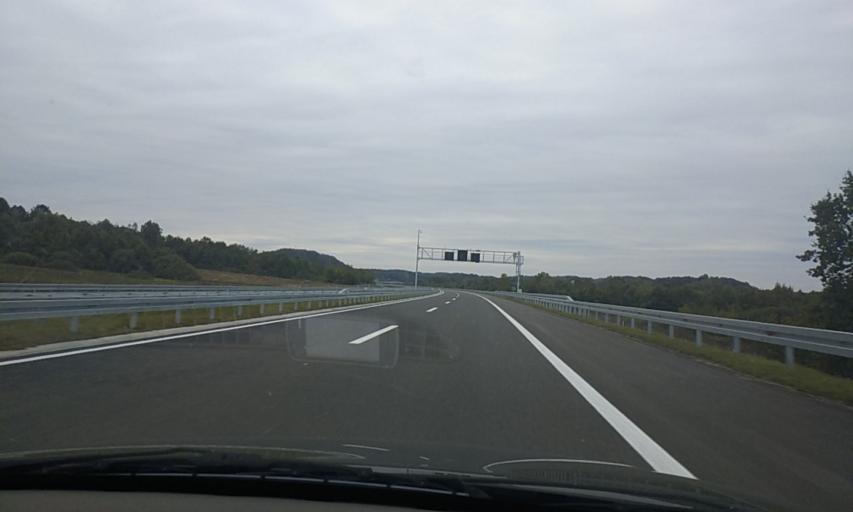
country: BA
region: Republika Srpska
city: Prnjavor
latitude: 44.8811
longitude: 17.6212
